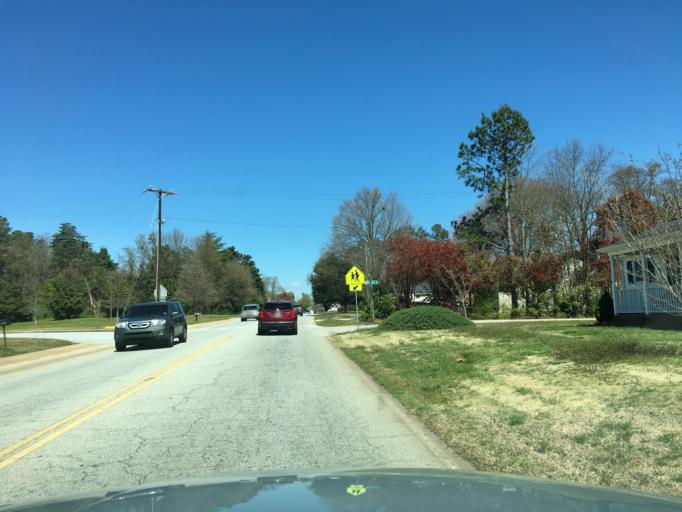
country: US
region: South Carolina
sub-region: Spartanburg County
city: Fairforest
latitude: 34.9263
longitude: -82.0014
